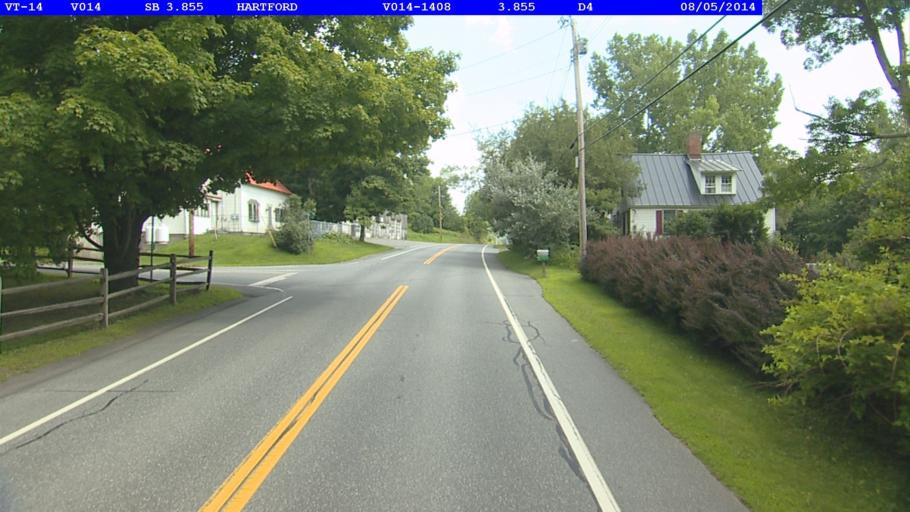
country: US
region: Vermont
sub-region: Windsor County
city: White River Junction
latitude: 43.6764
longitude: -72.3868
